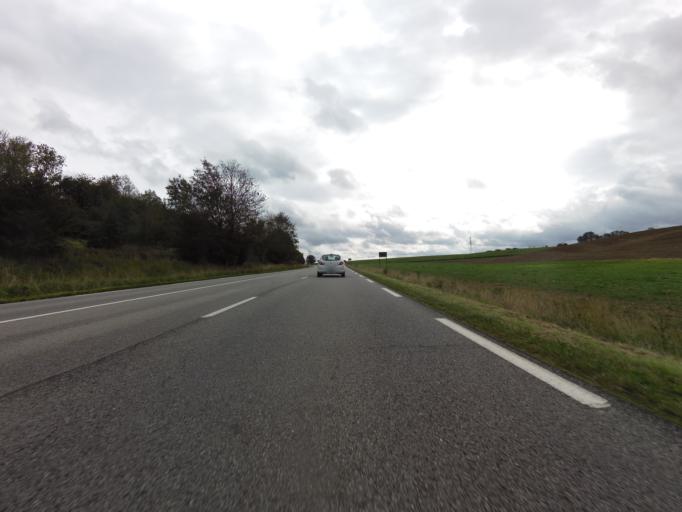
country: FR
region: Haute-Normandie
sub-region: Departement de la Seine-Maritime
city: Criel-sur-Mer
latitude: 50.0209
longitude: 1.3492
